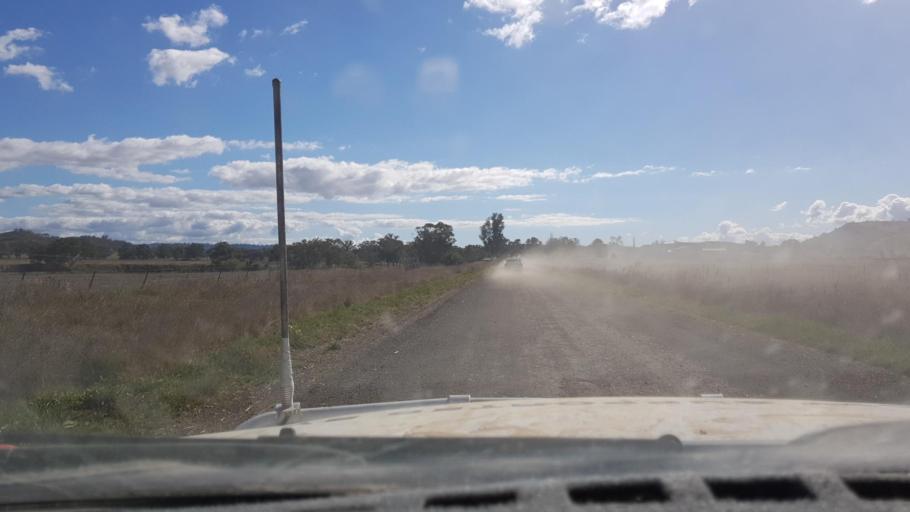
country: AU
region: New South Wales
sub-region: Narrabri
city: Blair Athol
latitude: -30.4546
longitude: 150.4496
